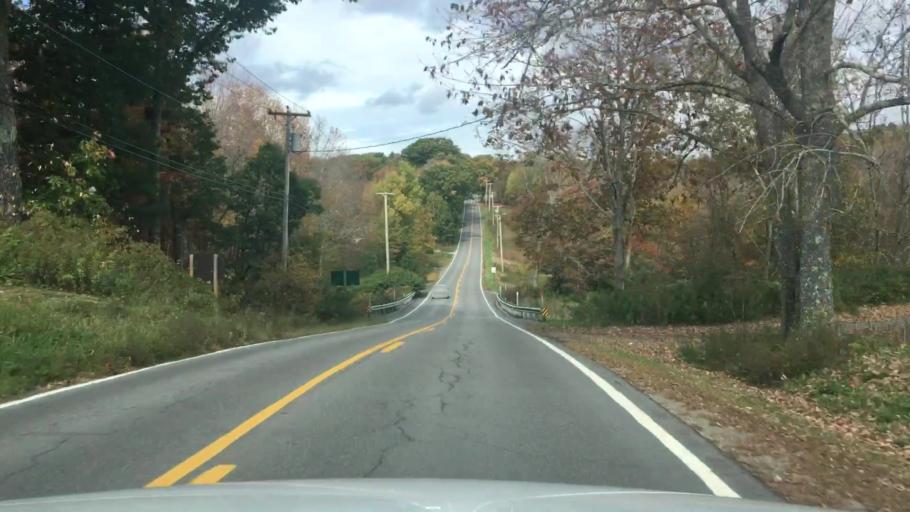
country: US
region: Maine
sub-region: Knox County
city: Hope
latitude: 44.2992
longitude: -69.1088
